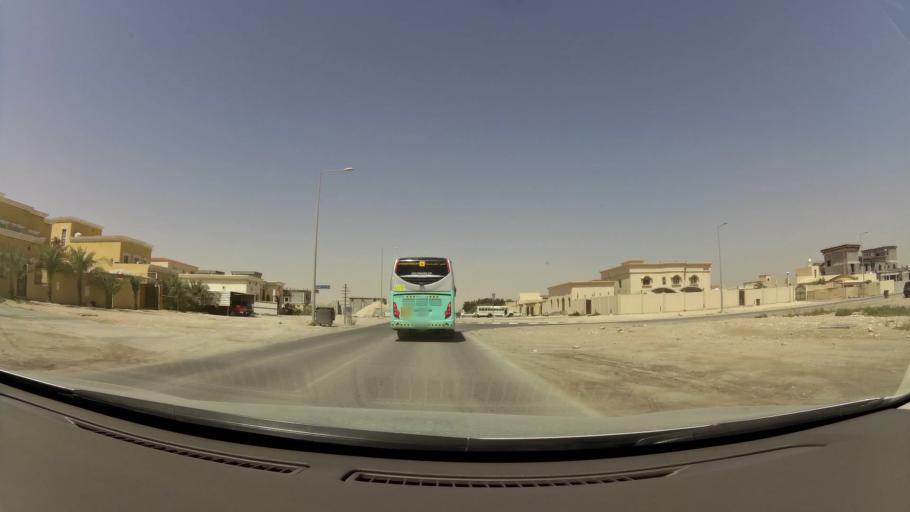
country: QA
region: Baladiyat ar Rayyan
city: Ar Rayyan
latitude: 25.2528
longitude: 51.4024
